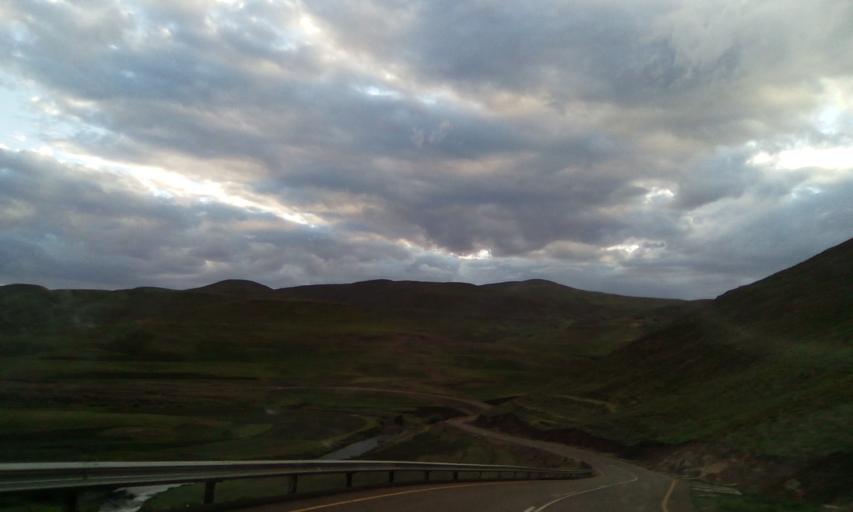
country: LS
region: Maseru
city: Nako
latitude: -29.8030
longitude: 28.0324
